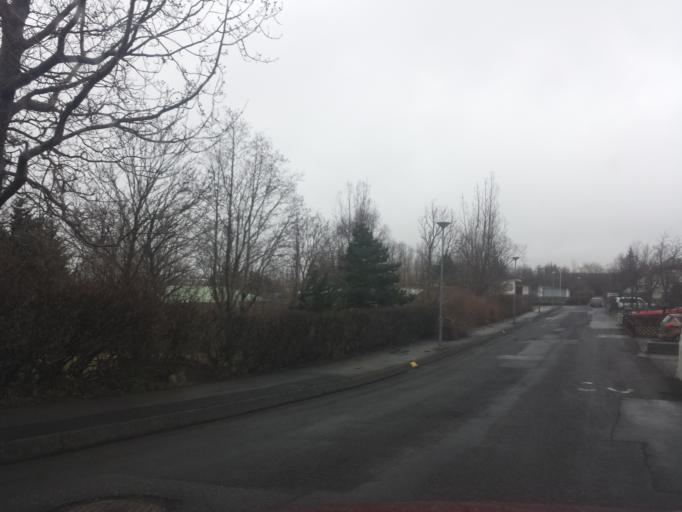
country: IS
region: Capital Region
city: Reykjavik
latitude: 64.1124
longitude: -21.8576
